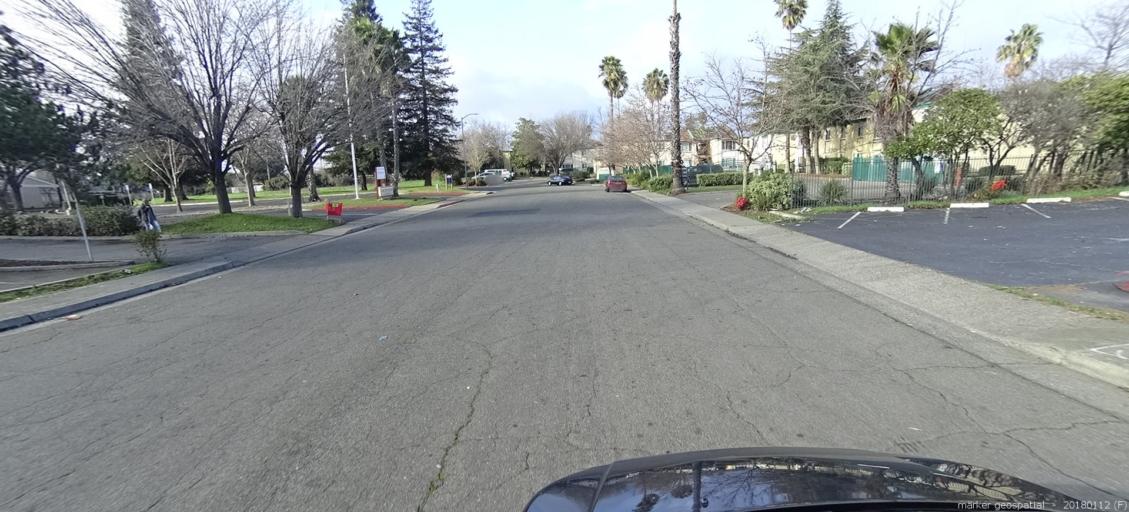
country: US
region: California
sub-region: Sacramento County
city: Rancho Cordova
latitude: 38.5910
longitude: -121.3001
